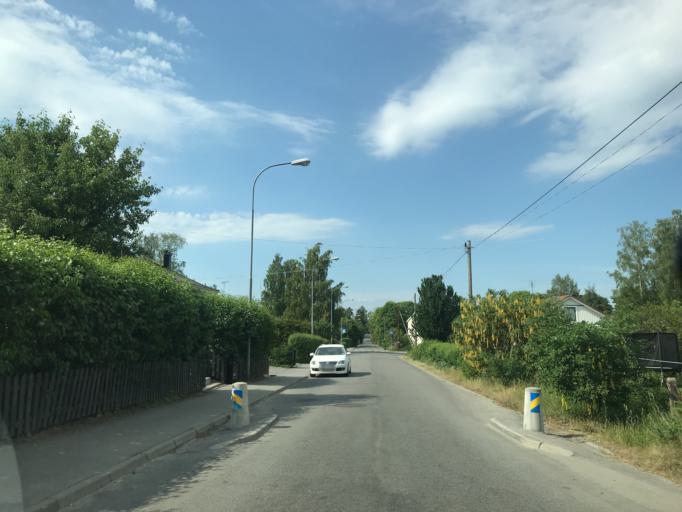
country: SE
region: Stockholm
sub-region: Sollentuna Kommun
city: Sollentuna
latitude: 59.4139
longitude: 17.9602
